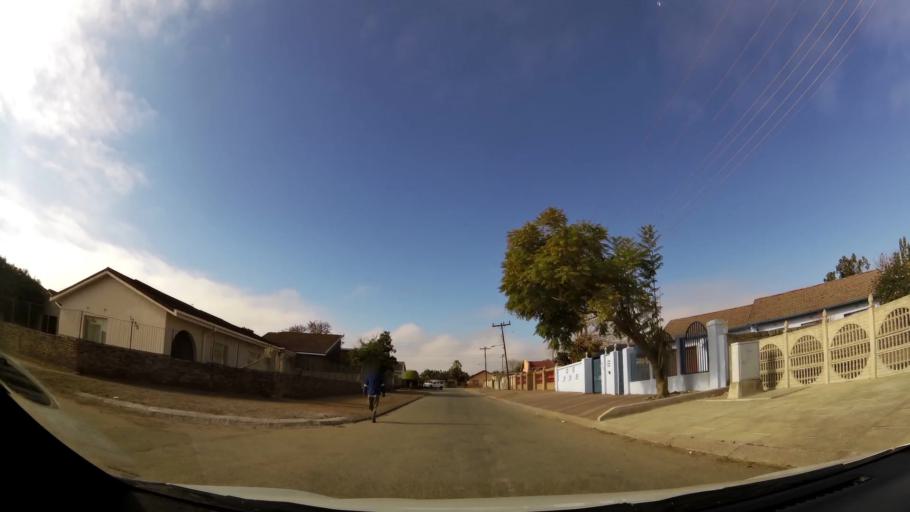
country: ZA
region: Limpopo
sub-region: Capricorn District Municipality
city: Polokwane
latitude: -23.8464
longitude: 29.3827
